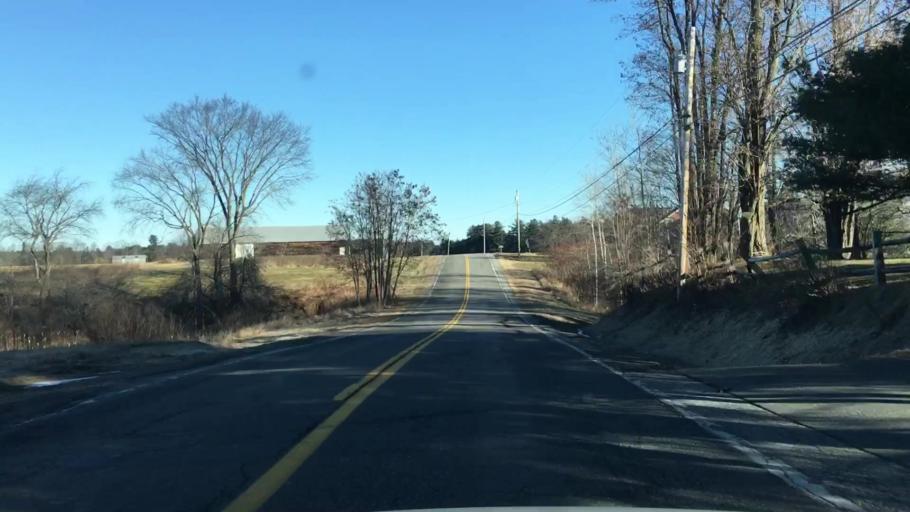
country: US
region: Maine
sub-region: Somerset County
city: Fairfield
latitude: 44.5586
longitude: -69.5815
